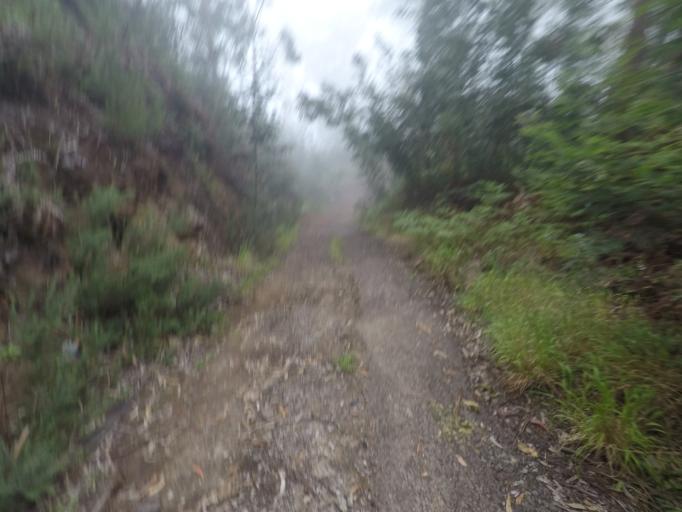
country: PT
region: Madeira
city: Ponta do Sol
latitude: 32.7127
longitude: -17.0928
